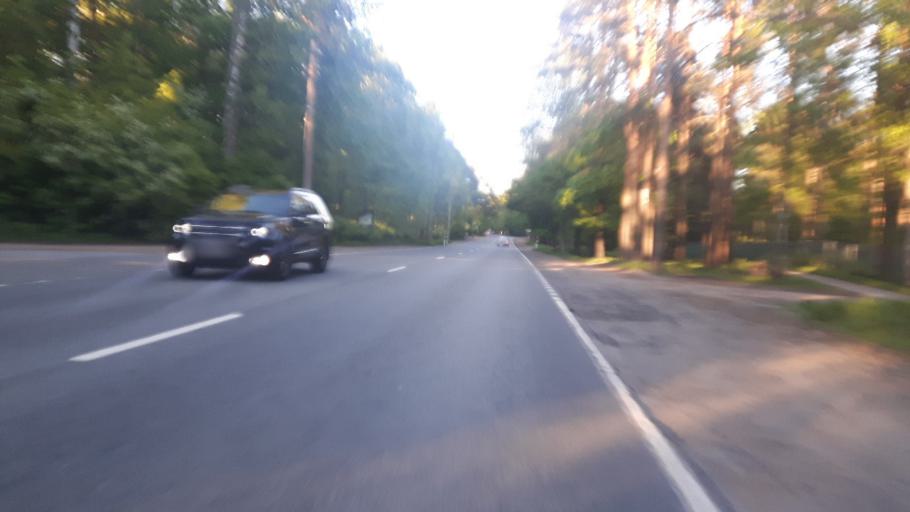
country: RU
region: St.-Petersburg
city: Zelenogorsk
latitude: 60.1930
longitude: 29.6604
